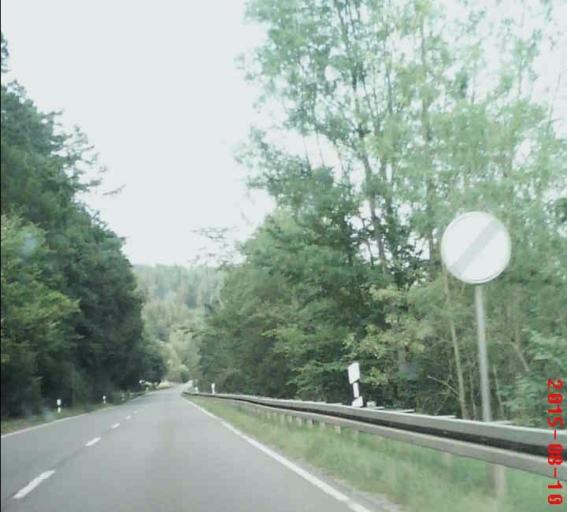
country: DE
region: Thuringia
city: Dillstadt
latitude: 50.5907
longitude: 10.5468
